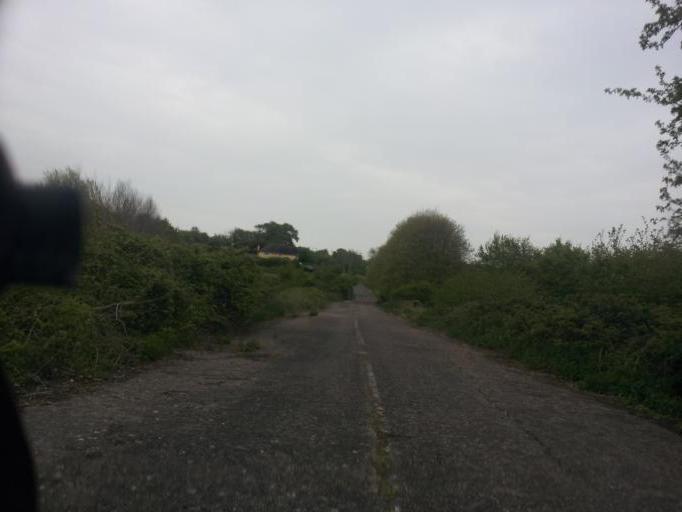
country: GB
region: England
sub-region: Medway
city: High Halstow
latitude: 51.4390
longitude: 0.5726
